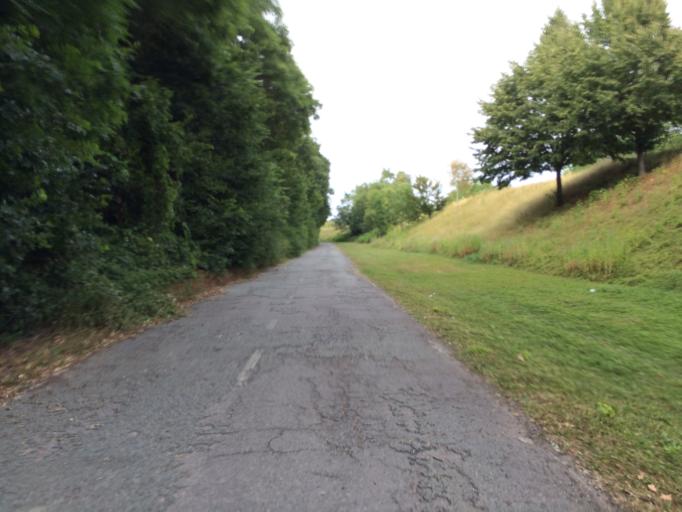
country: FR
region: Ile-de-France
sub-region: Departement de l'Essonne
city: Quincy-sous-Senart
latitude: 48.6568
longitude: 2.5478
